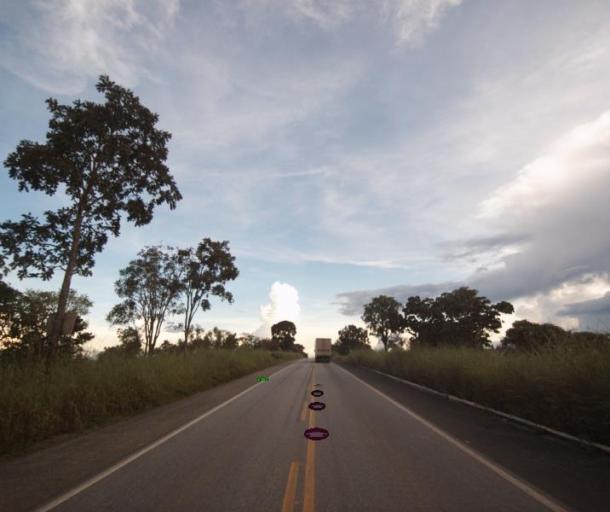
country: BR
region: Goias
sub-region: Uruacu
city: Uruacu
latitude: -14.2468
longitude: -49.1385
